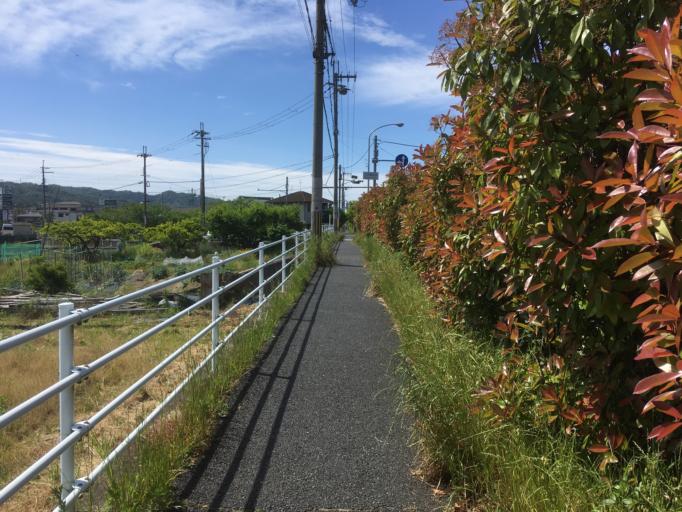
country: JP
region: Nara
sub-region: Ikoma-shi
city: Ikoma
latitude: 34.6789
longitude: 135.7063
